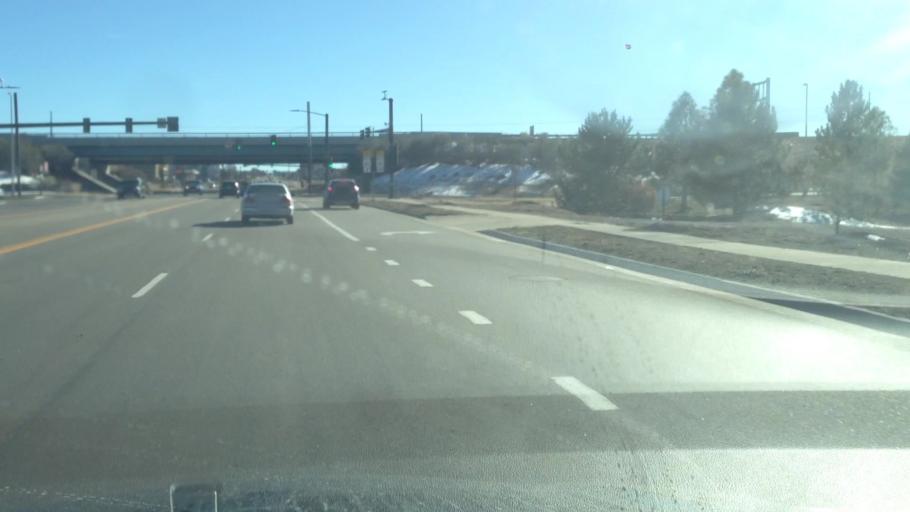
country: US
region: Colorado
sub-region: Douglas County
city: Stonegate
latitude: 39.5506
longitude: -104.7934
